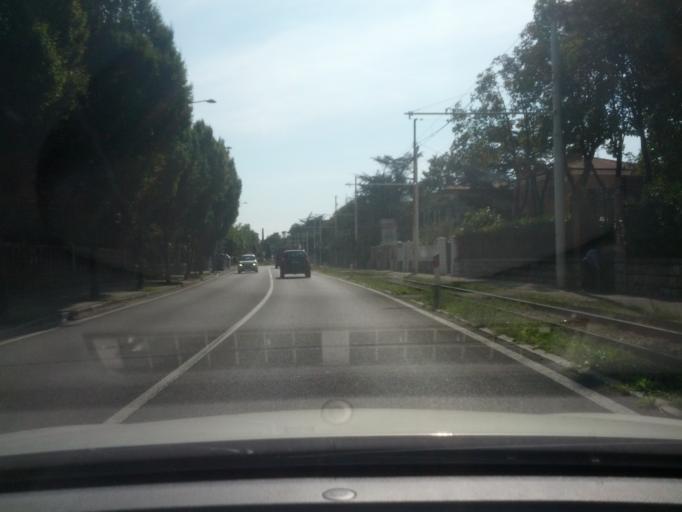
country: IT
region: Friuli Venezia Giulia
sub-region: Provincia di Trieste
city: Villa Opicina
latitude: 45.6845
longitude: 13.7846
